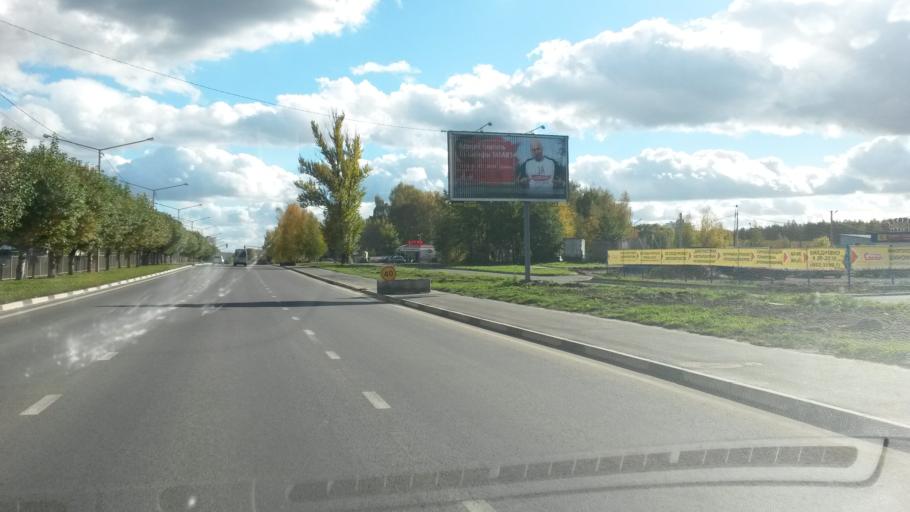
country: RU
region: Jaroslavl
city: Yaroslavl
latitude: 57.5794
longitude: 39.9131
